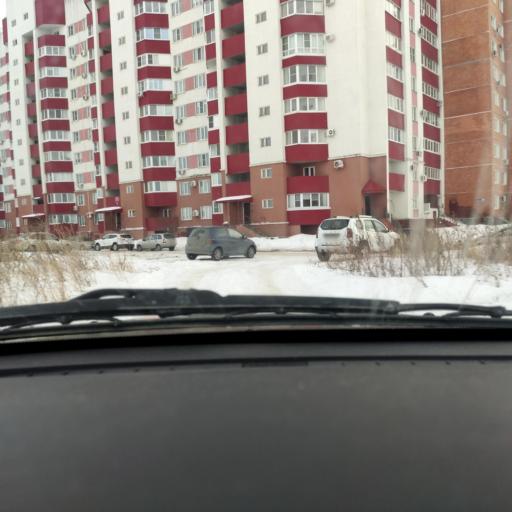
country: RU
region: Samara
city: Tol'yatti
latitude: 53.5430
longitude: 49.4017
